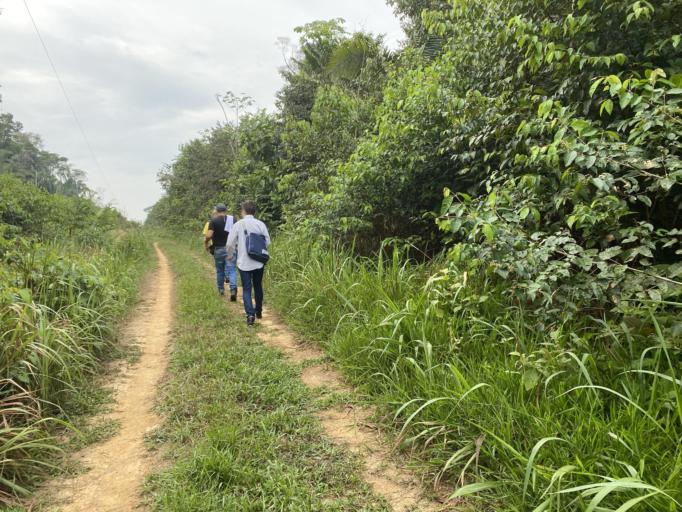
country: BR
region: Rondonia
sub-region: Porto Velho
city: Porto Velho
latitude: -8.8344
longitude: -64.2319
